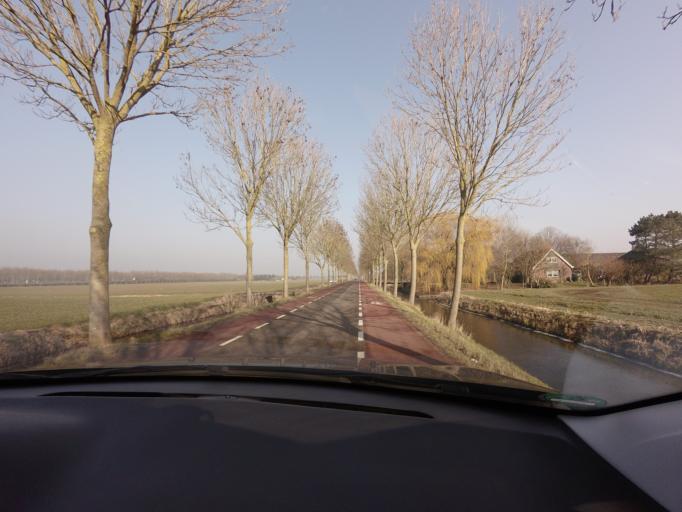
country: NL
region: North Holland
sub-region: Gemeente Beemster
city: Halfweg
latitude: 52.5485
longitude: 4.9627
